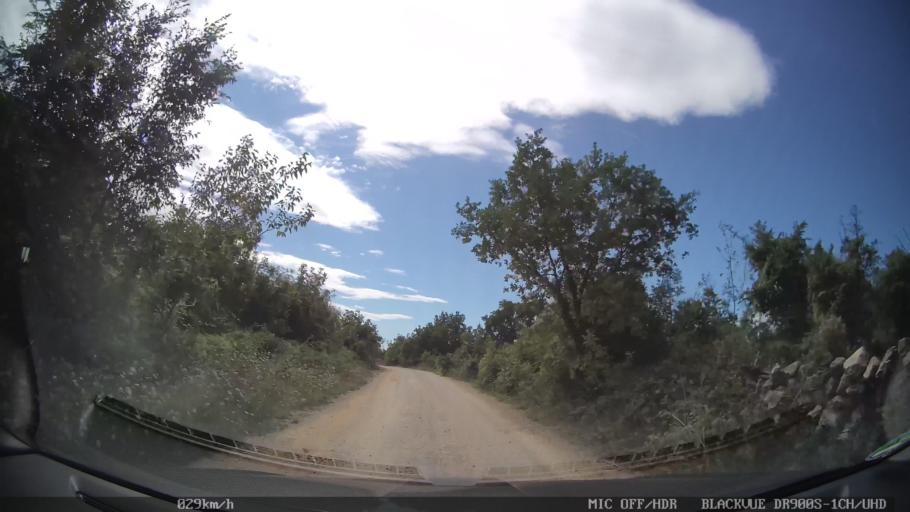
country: HR
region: Primorsko-Goranska
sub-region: Grad Krk
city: Krk
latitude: 45.0432
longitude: 14.5298
